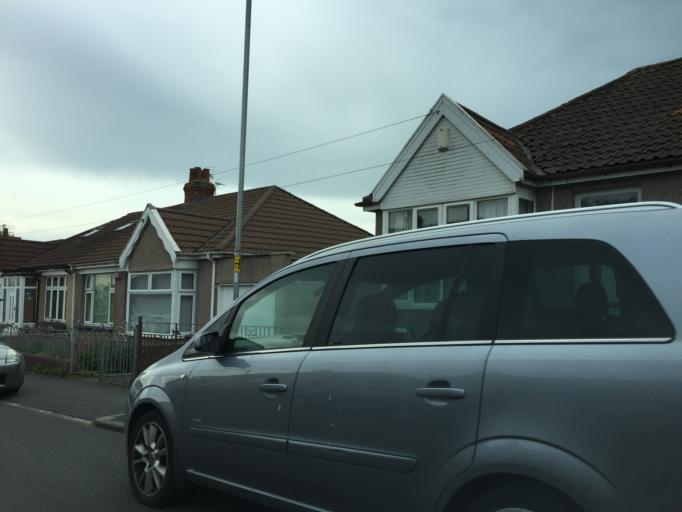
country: GB
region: England
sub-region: South Gloucestershire
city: Stoke Gifford
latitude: 51.5011
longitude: -2.5750
